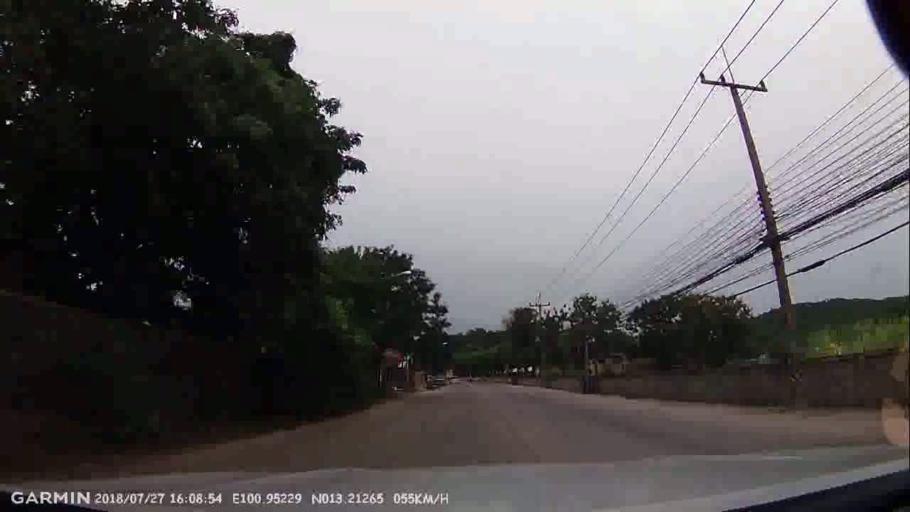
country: TH
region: Chon Buri
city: Si Racha
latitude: 13.2126
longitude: 100.9524
